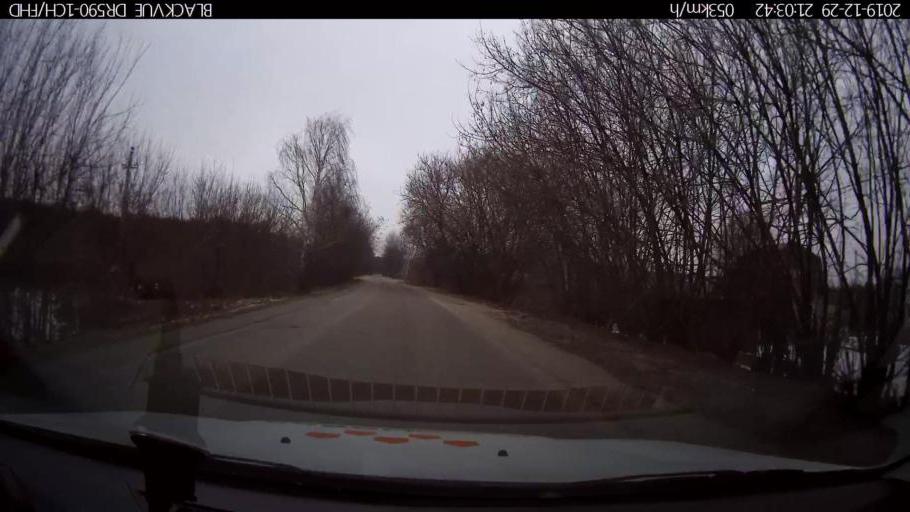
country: RU
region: Nizjnij Novgorod
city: Afonino
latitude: 56.1973
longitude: 44.0061
